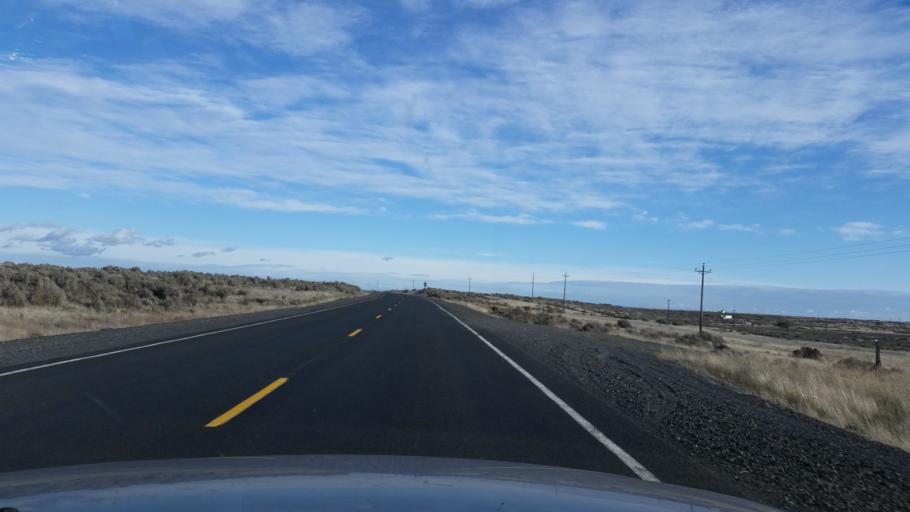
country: US
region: Washington
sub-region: Adams County
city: Ritzville
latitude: 47.3133
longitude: -118.7560
